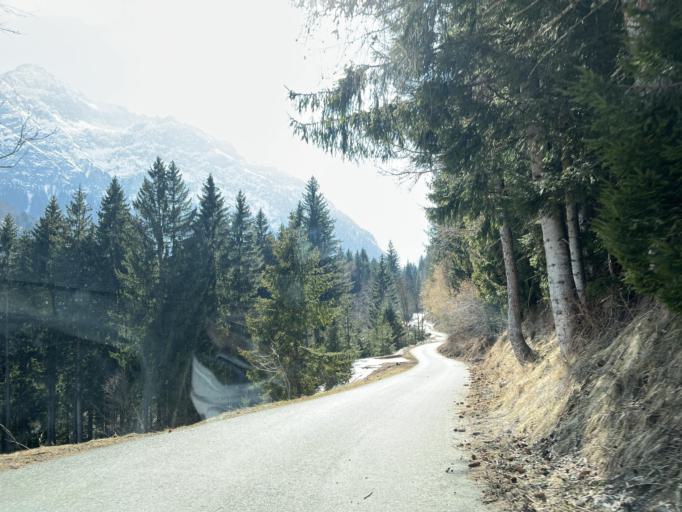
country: AT
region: Carinthia
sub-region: Politischer Bezirk Spittal an der Drau
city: Oberdrauburg
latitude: 46.6544
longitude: 12.9760
